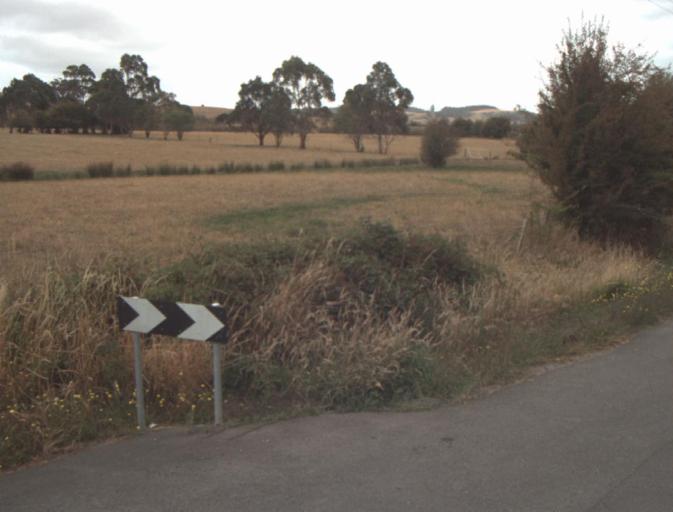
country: AU
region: Tasmania
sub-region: Launceston
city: Mayfield
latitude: -41.2487
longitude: 147.2178
